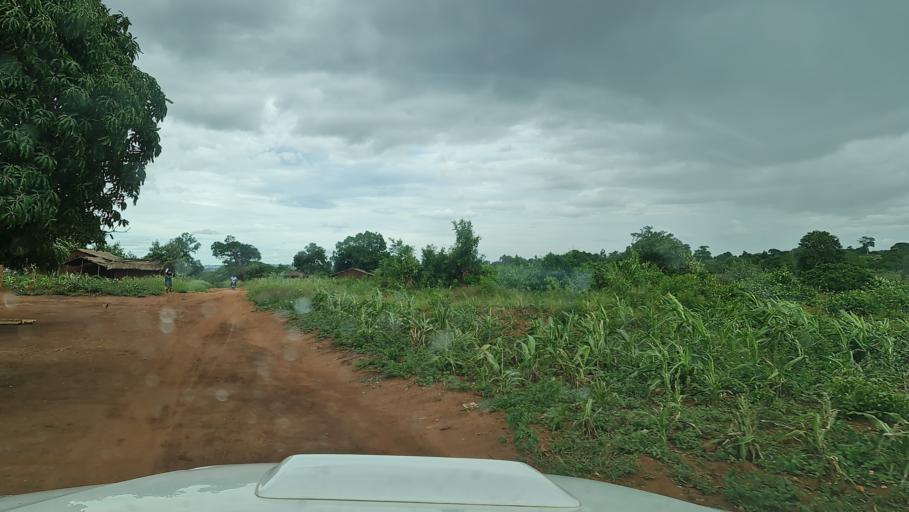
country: MZ
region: Nampula
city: Nacala
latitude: -14.7488
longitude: 40.0260
